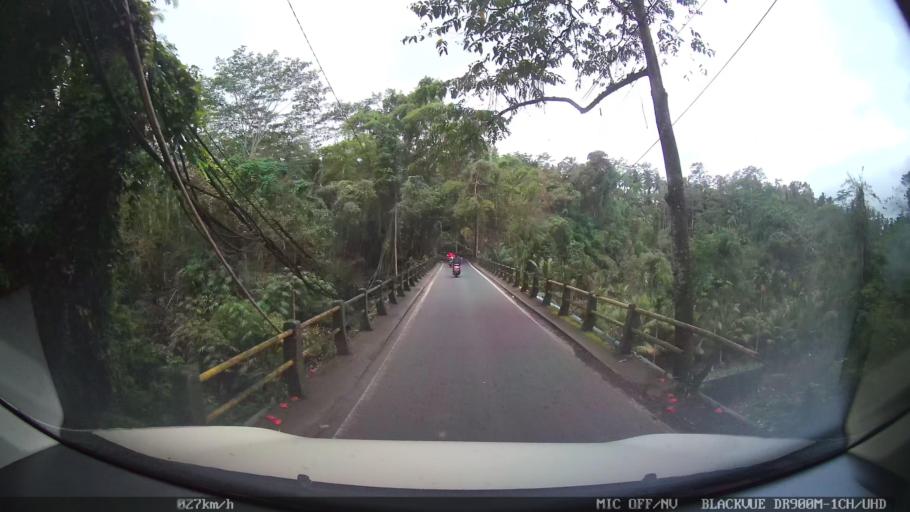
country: ID
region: Bali
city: Banjar Triwangsakeliki
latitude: -8.4467
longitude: 115.2694
